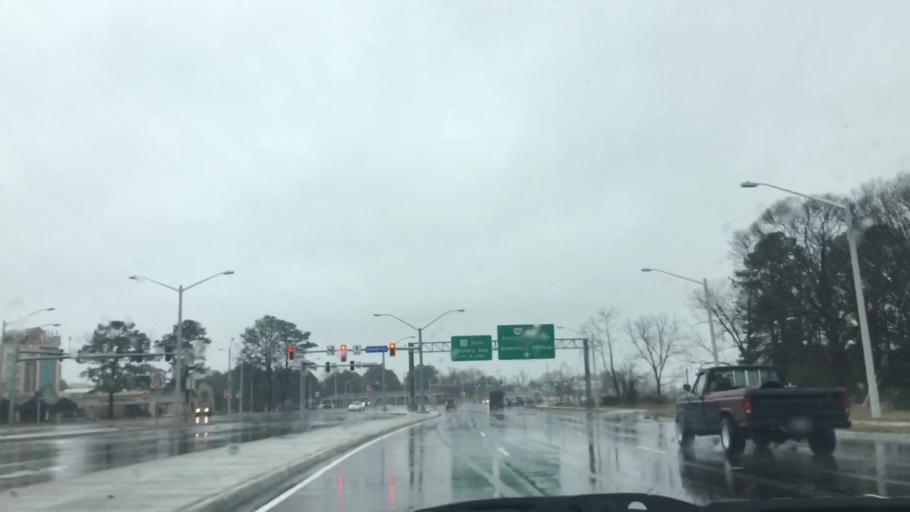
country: US
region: Virginia
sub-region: City of Norfolk
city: Norfolk
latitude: 36.8773
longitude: -76.2113
